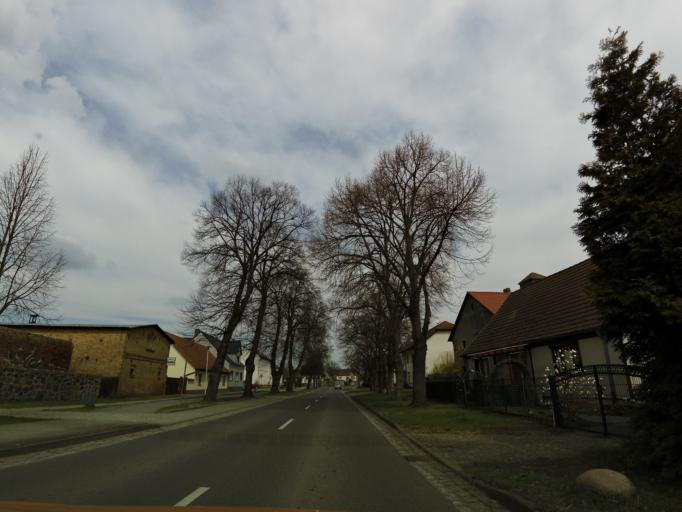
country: DE
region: Brandenburg
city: Briesen
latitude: 52.3434
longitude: 14.2768
